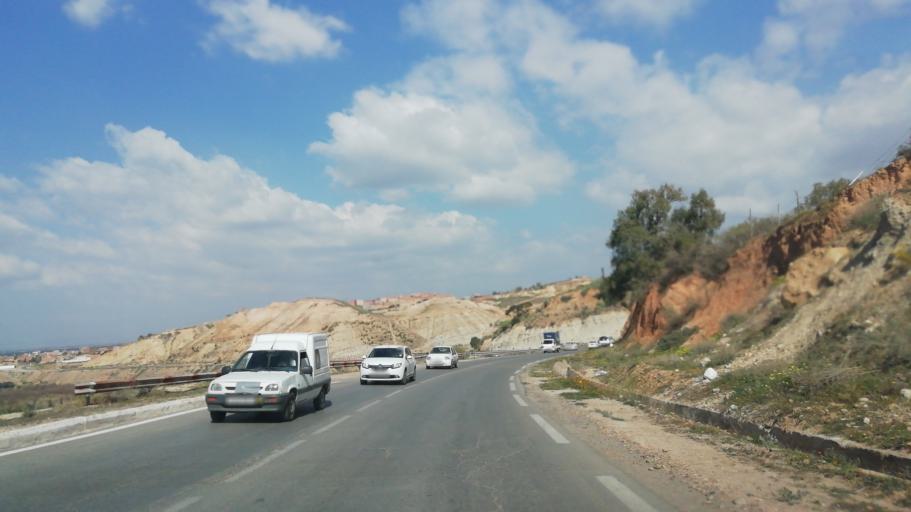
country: DZ
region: Mascara
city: Mascara
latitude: 35.5609
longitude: 0.0695
